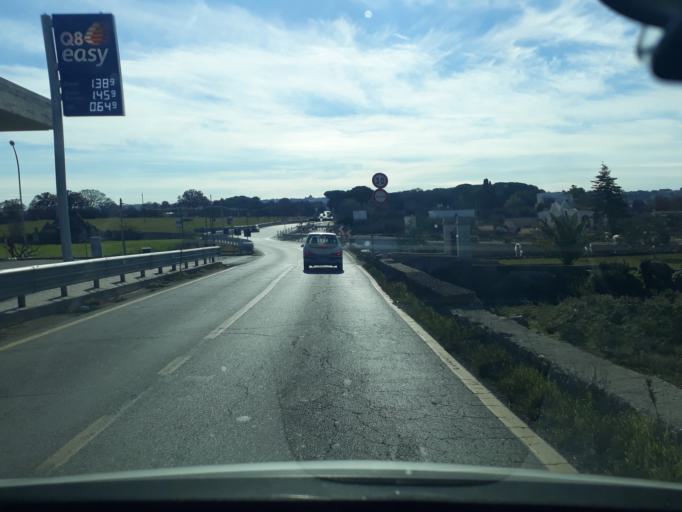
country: IT
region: Apulia
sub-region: Provincia di Bari
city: Locorotondo
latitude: 40.7373
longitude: 17.3326
